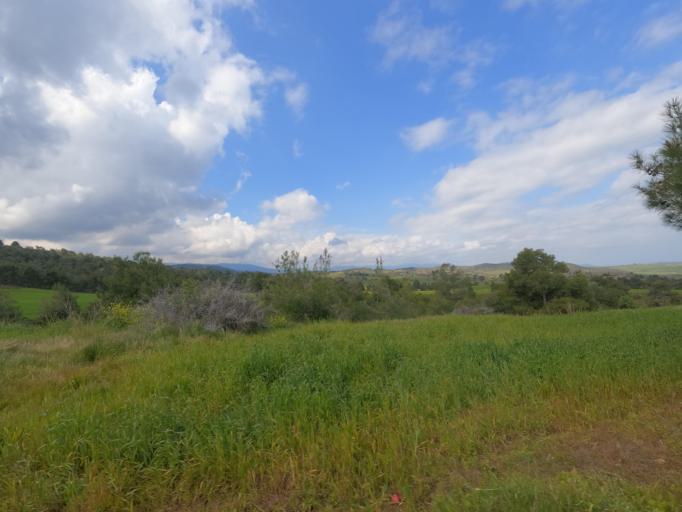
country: CY
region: Lefkosia
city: Astromeritis
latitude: 35.0753
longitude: 32.9619
